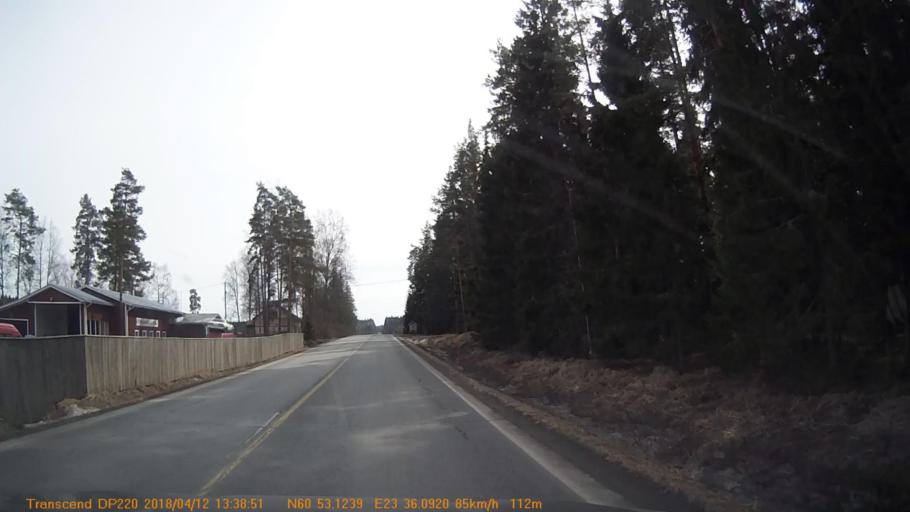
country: FI
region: Haeme
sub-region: Forssa
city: Forssa
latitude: 60.8851
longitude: 23.6017
